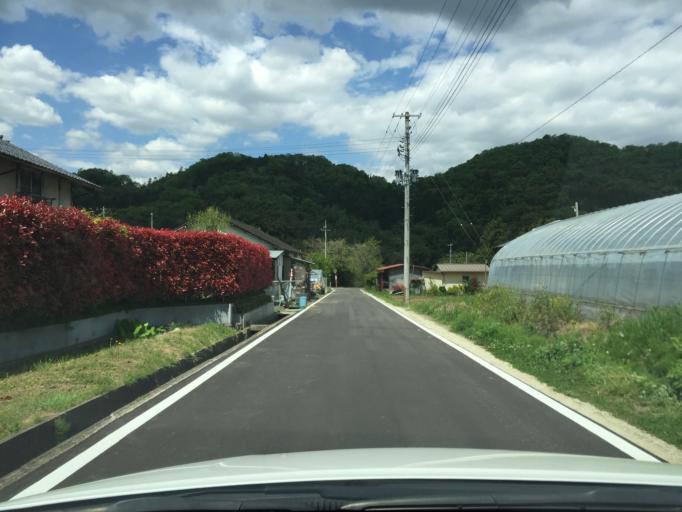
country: JP
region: Fukushima
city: Hobaramachi
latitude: 37.7475
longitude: 140.5669
